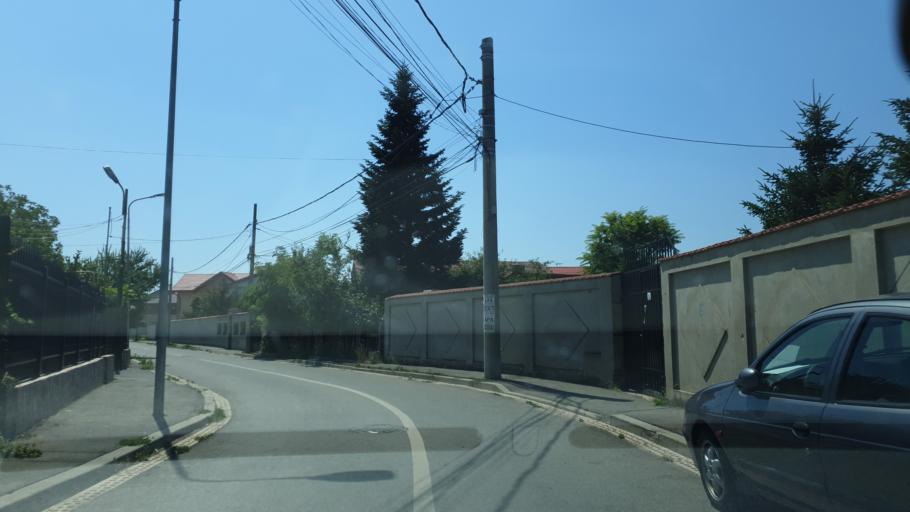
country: RO
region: Ilfov
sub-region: Comuna Chiajna
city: Rosu
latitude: 44.4669
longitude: 26.0218
